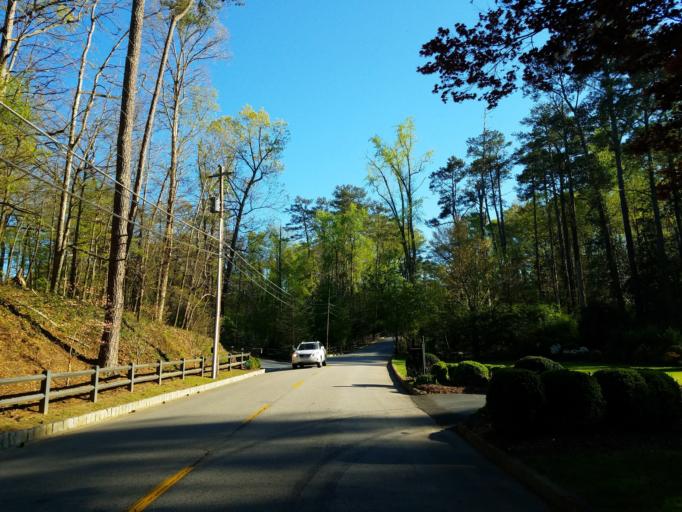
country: US
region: Georgia
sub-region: Cobb County
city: Vinings
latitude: 33.8422
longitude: -84.4406
